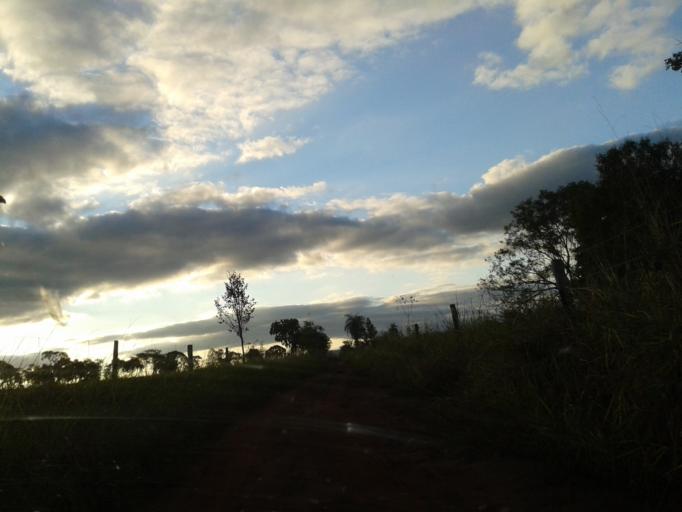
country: BR
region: Minas Gerais
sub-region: Campina Verde
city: Campina Verde
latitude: -19.5108
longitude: -49.6789
